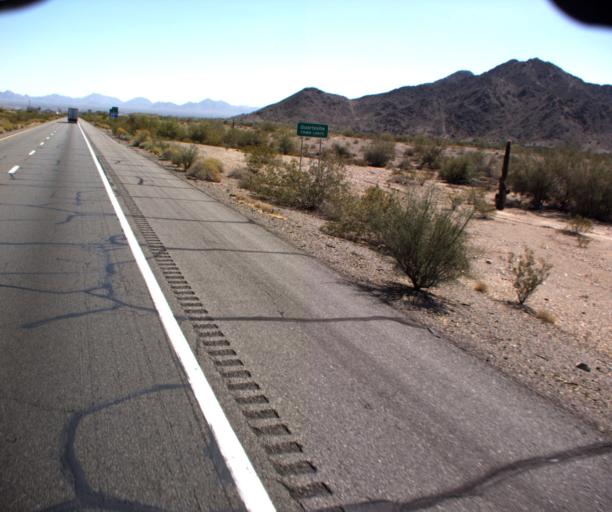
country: US
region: Arizona
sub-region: La Paz County
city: Quartzsite
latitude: 33.6553
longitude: -114.2712
